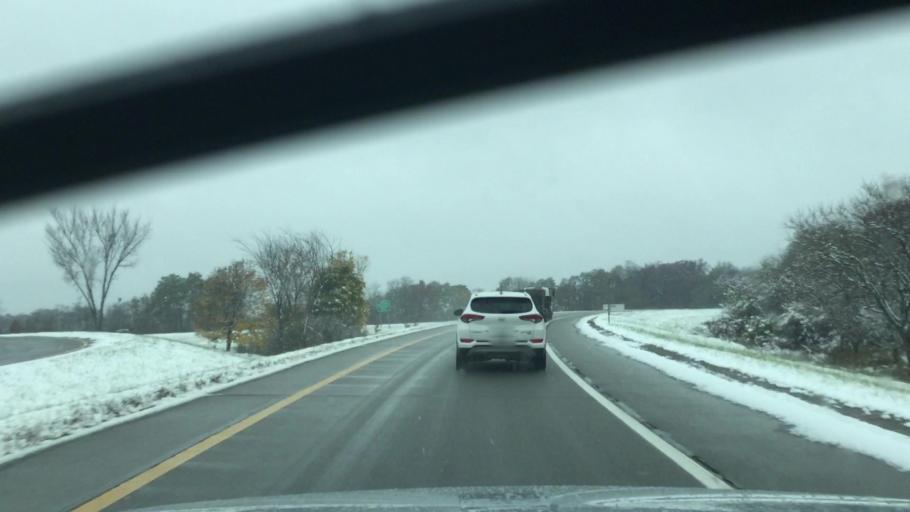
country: US
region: Michigan
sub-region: Oakland County
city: Auburn Hills
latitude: 42.6429
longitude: -83.2364
